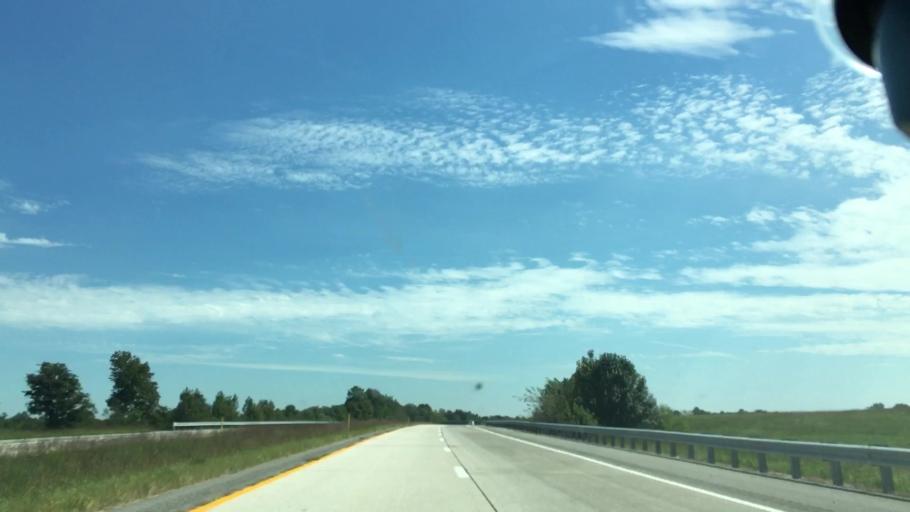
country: US
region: Kentucky
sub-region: Henderson County
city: Henderson
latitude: 37.7729
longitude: -87.4345
